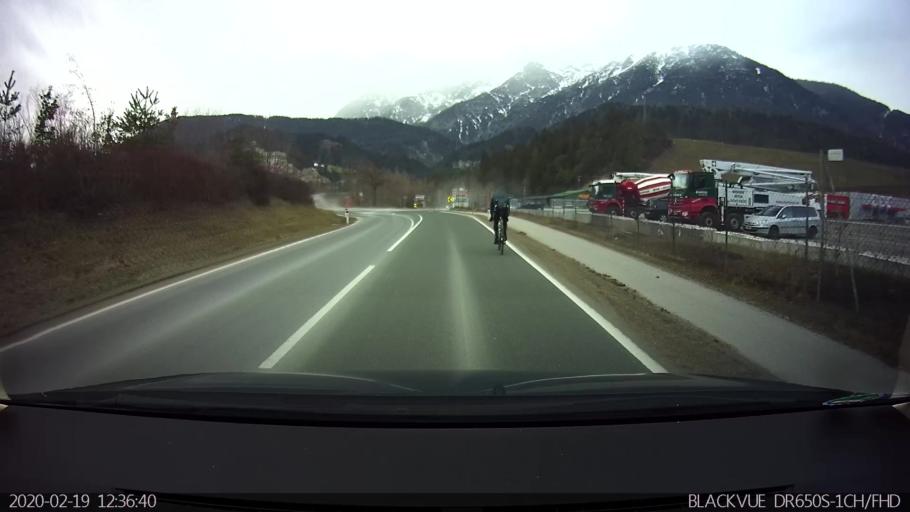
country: AT
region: Tyrol
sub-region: Politischer Bezirk Schwaz
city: Vomp
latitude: 47.3301
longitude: 11.6698
